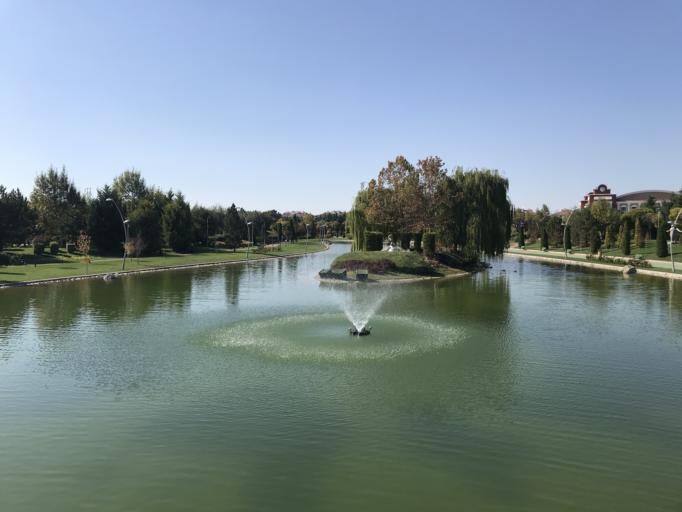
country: TR
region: Eskisehir
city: Eskisehir
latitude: 39.7739
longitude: 30.5492
